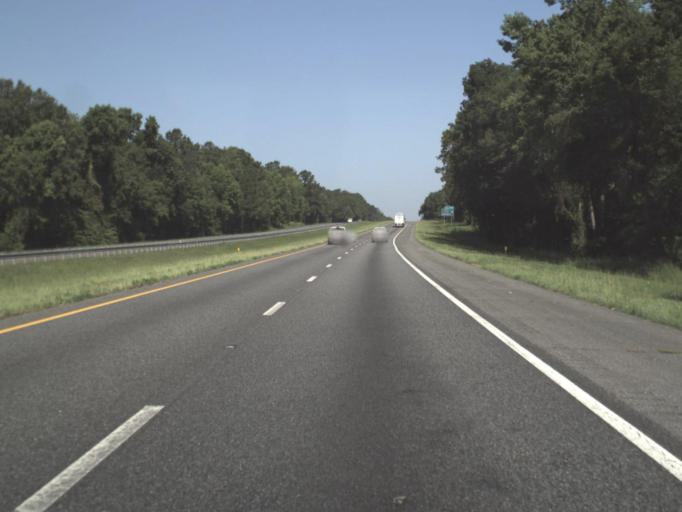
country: US
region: Florida
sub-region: Suwannee County
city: Wellborn
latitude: 30.2767
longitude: -82.8085
